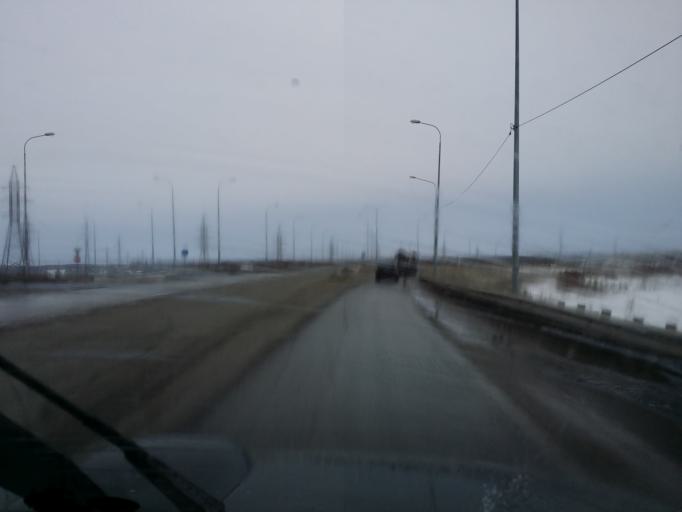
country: RU
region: Khanty-Mansiyskiy Avtonomnyy Okrug
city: Nizhnevartovsk
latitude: 60.9500
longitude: 76.6635
